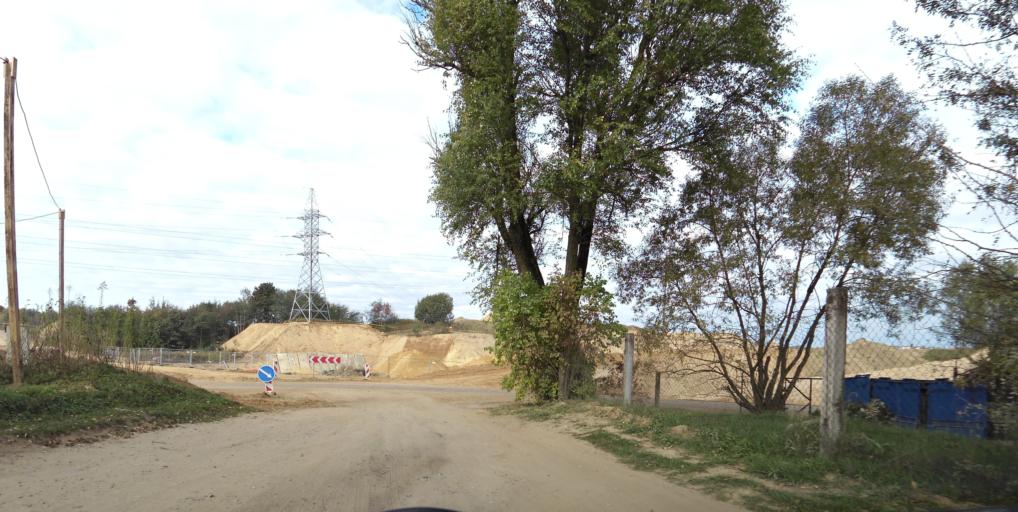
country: LT
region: Vilnius County
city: Justiniskes
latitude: 54.7210
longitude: 25.2091
